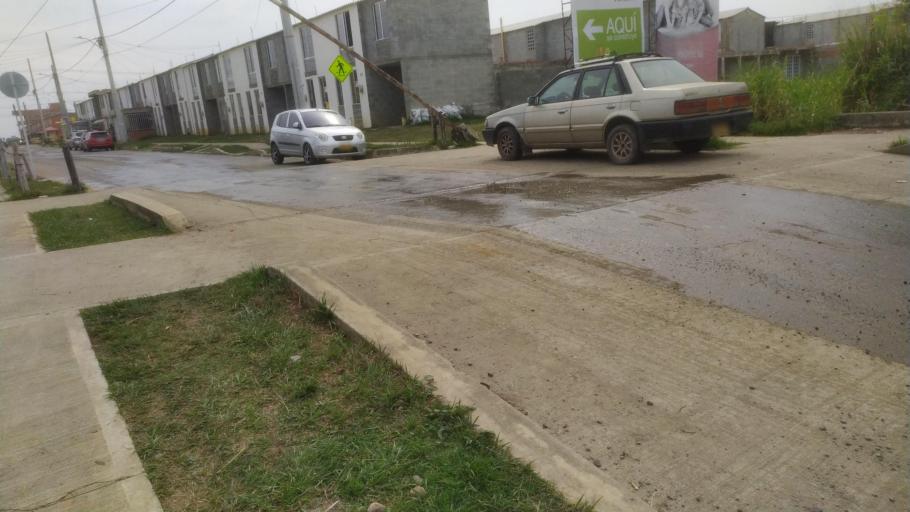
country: CO
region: Valle del Cauca
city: Jamundi
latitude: 3.2387
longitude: -76.5066
